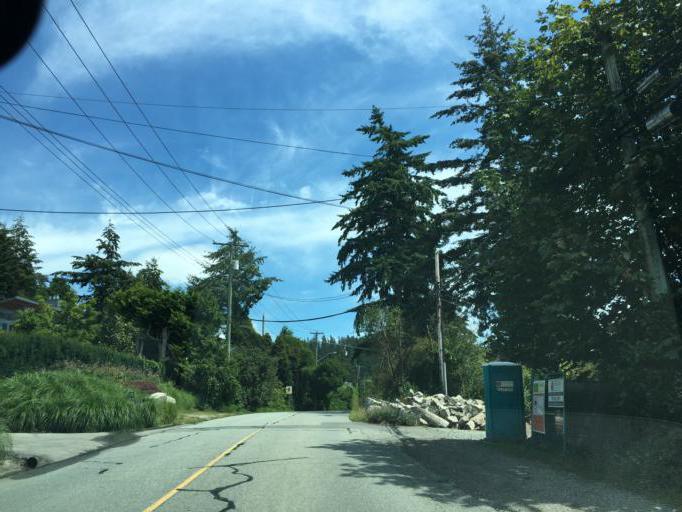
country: CA
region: British Columbia
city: West Vancouver
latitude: 49.3416
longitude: -123.2316
